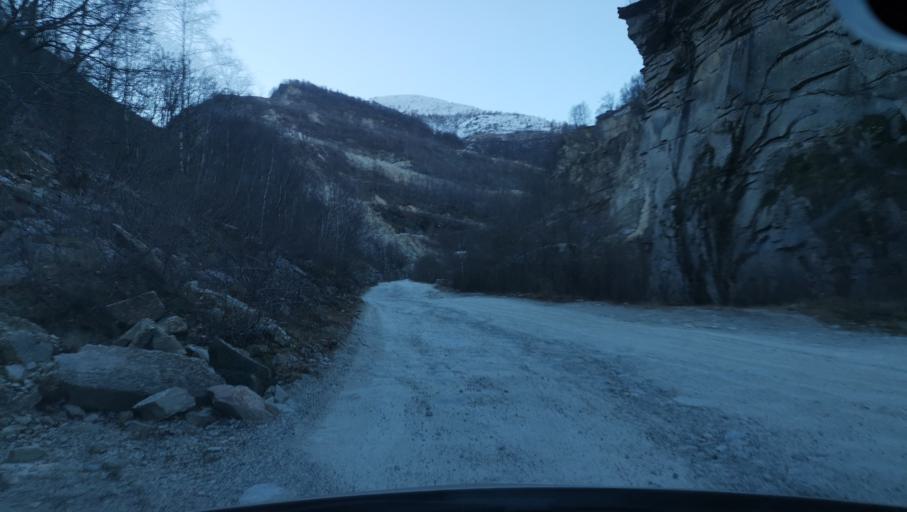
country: IT
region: Piedmont
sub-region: Provincia di Torino
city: Rora
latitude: 44.7656
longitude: 7.2006
